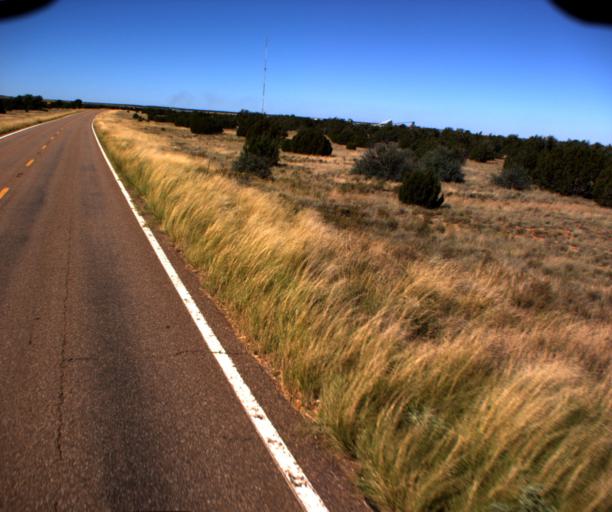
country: US
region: Arizona
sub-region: Navajo County
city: Heber-Overgaard
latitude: 34.4610
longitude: -110.3912
